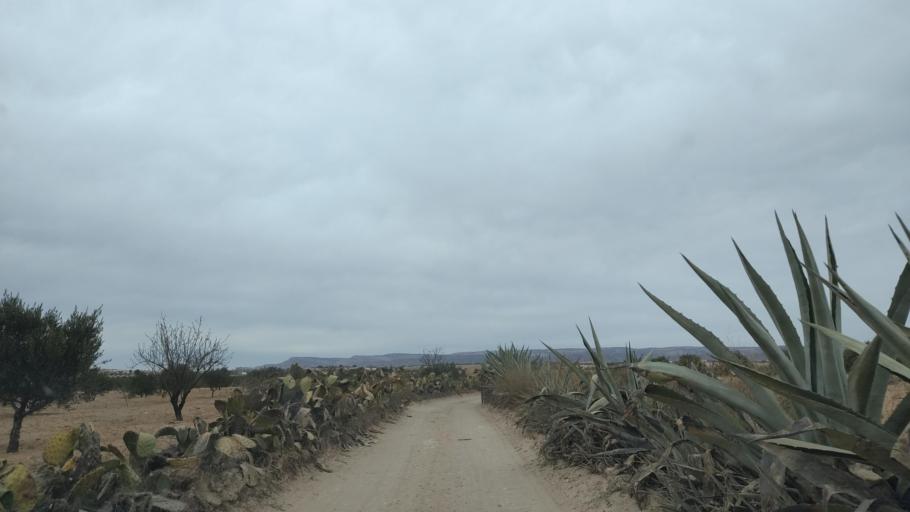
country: TN
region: Al Qasrayn
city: Kasserine
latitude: 35.2257
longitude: 8.9224
